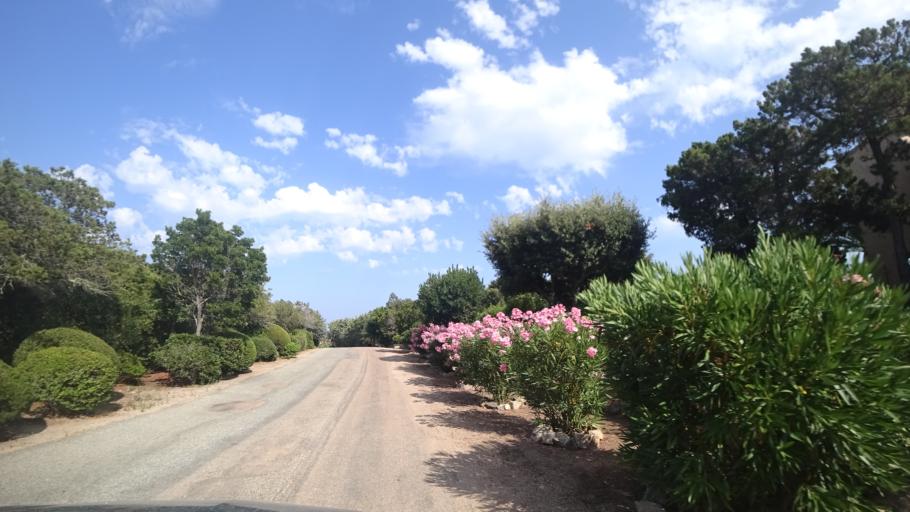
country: FR
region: Corsica
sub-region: Departement de la Corse-du-Sud
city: Porto-Vecchio
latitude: 41.6198
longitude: 9.3471
